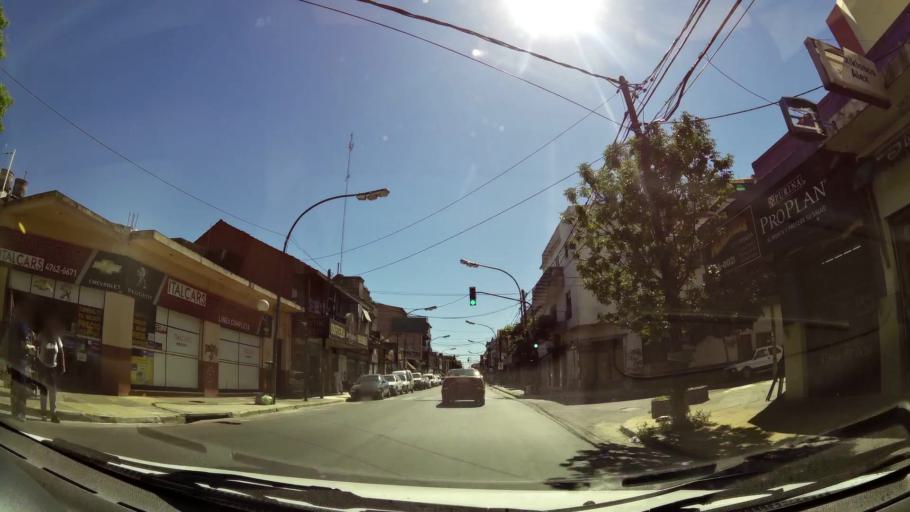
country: AR
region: Buenos Aires
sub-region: Partido de General San Martin
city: General San Martin
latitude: -34.5326
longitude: -58.5287
